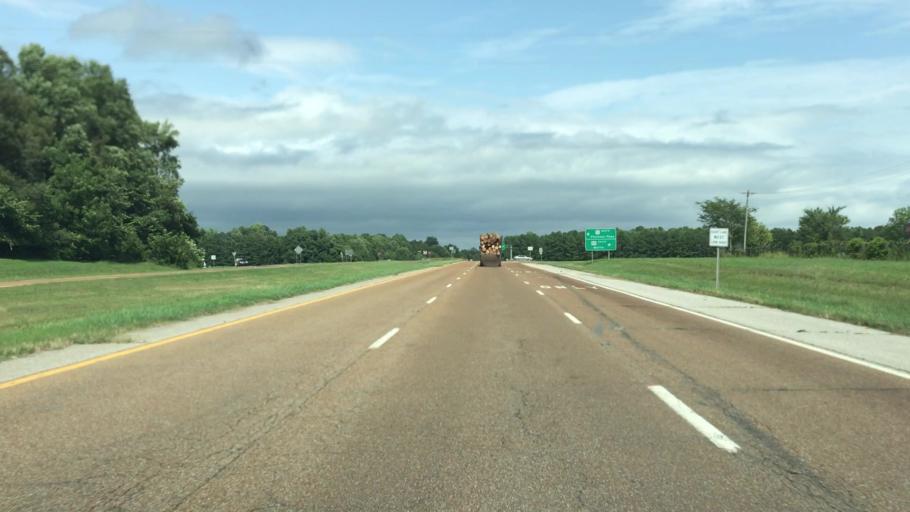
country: US
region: Tennessee
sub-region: Obion County
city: South Fulton
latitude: 36.4969
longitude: -88.9022
